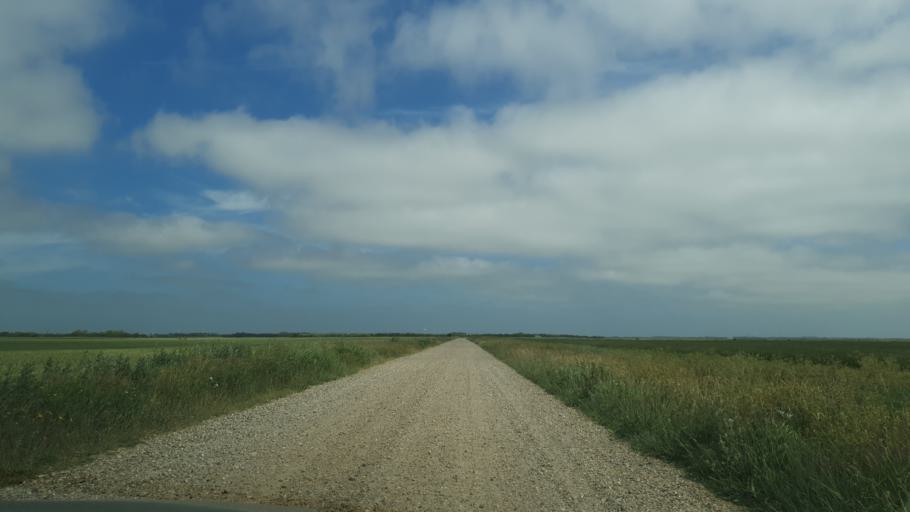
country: DK
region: Central Jutland
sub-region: Ringkobing-Skjern Kommune
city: Skjern
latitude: 55.9351
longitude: 8.4272
